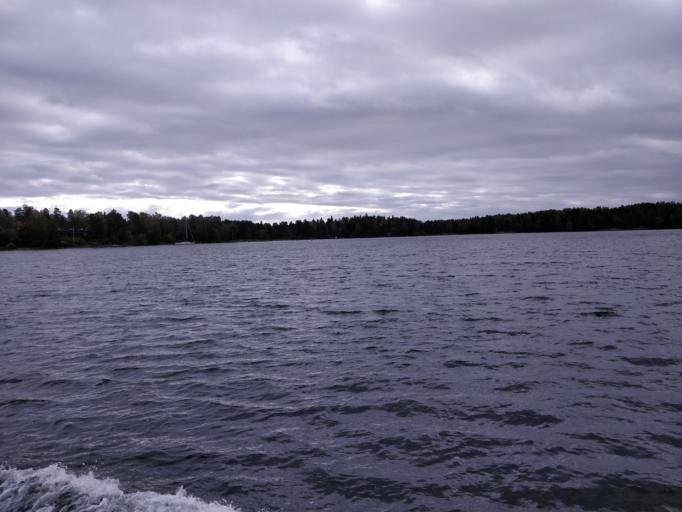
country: FI
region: Uusimaa
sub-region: Helsinki
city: Vantaa
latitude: 60.1754
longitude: 25.0789
